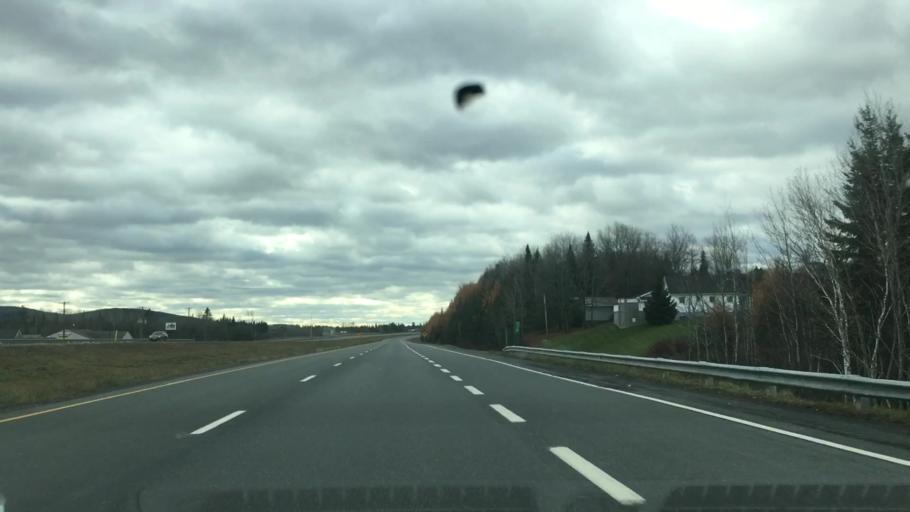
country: US
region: Maine
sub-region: Aroostook County
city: Fort Fairfield
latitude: 46.7479
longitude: -67.7147
